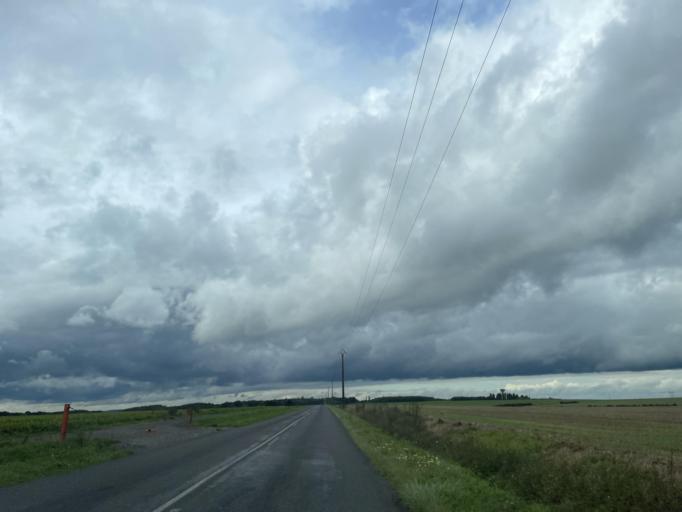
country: FR
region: Ile-de-France
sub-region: Departement de Seine-et-Marne
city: Saint-Jean-les-Deux-Jumeaux
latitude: 48.9258
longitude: 3.0015
